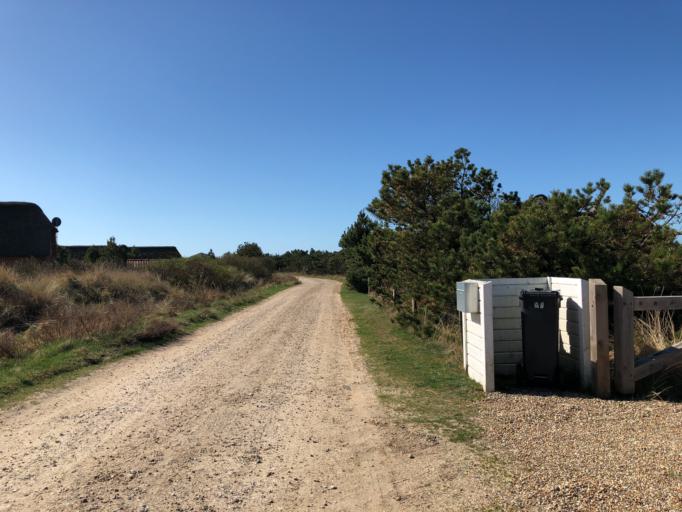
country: DK
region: South Denmark
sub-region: Varde Kommune
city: Oksbol
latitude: 55.5506
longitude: 8.1196
